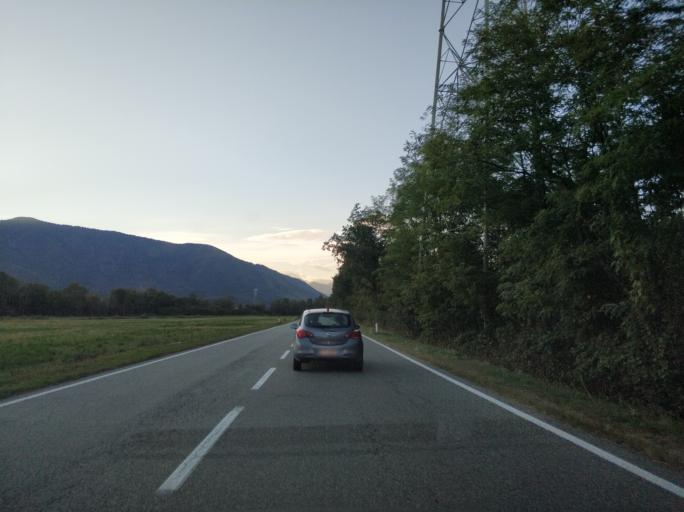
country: IT
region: Piedmont
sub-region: Provincia di Torino
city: Villanova Canavese
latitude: 45.2373
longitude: 7.5423
